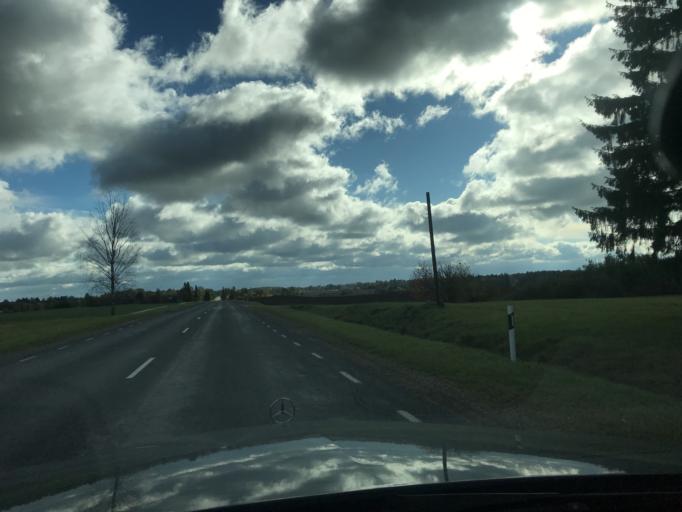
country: EE
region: Vorumaa
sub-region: Antsla vald
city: Vana-Antsla
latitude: 57.9527
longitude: 26.2826
